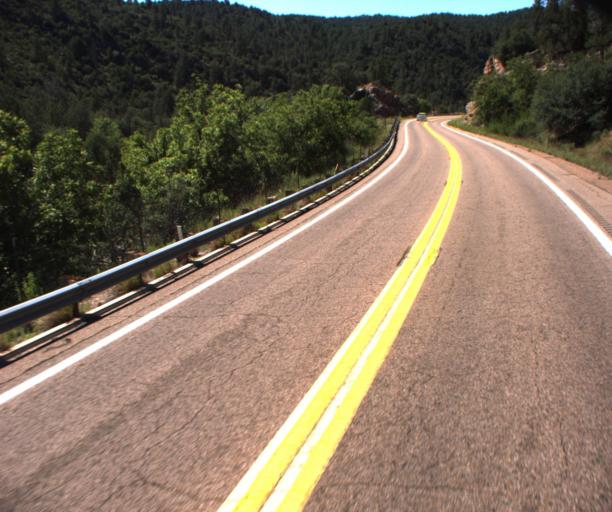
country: US
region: Arizona
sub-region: Navajo County
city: Cibecue
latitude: 33.8455
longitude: -110.4253
